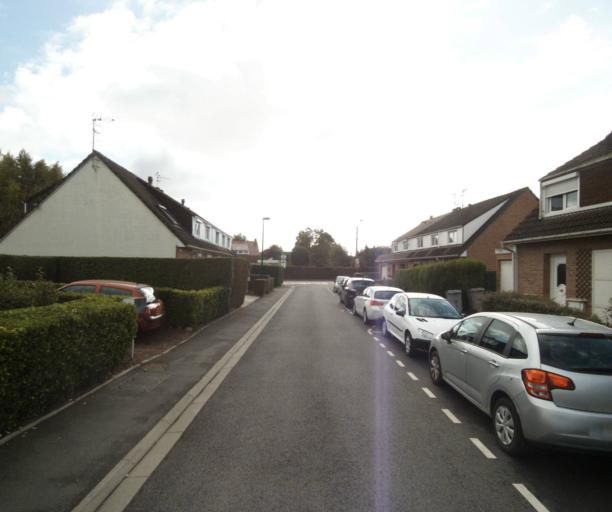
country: FR
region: Nord-Pas-de-Calais
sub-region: Departement du Nord
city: Verlinghem
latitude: 50.6829
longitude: 2.9983
